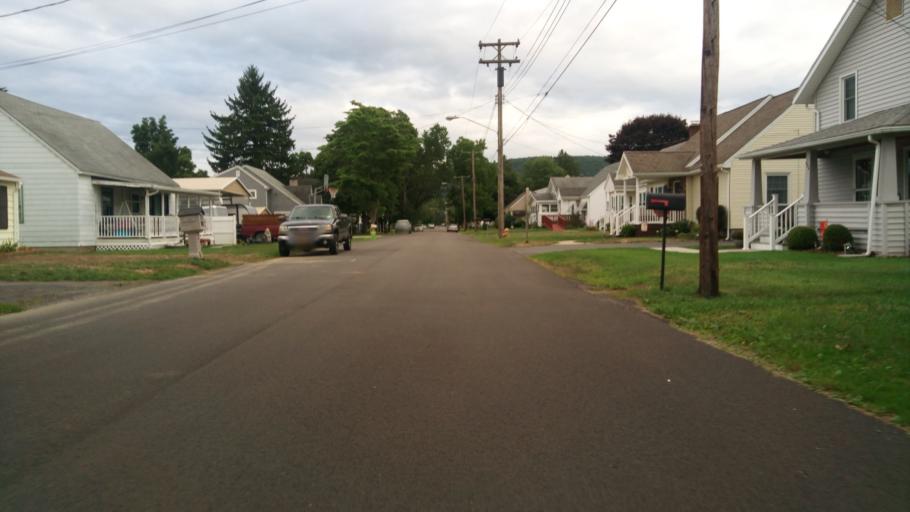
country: US
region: New York
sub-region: Chemung County
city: Southport
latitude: 42.0641
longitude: -76.8140
